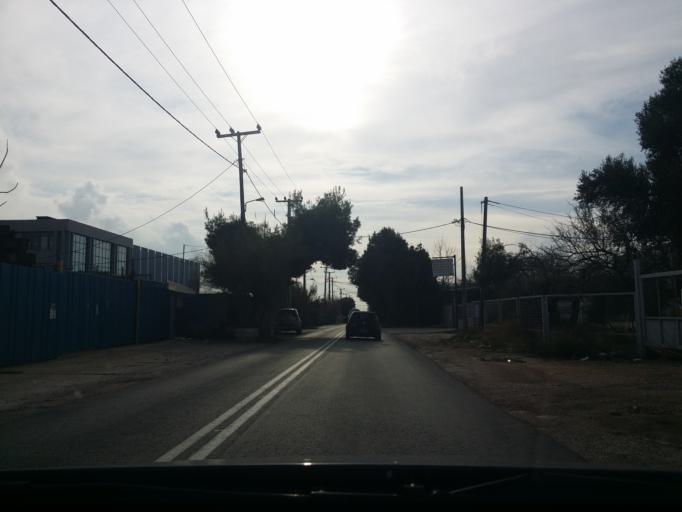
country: GR
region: Attica
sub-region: Nomarchia Athinas
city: Metamorfosi
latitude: 38.0891
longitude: 23.7713
